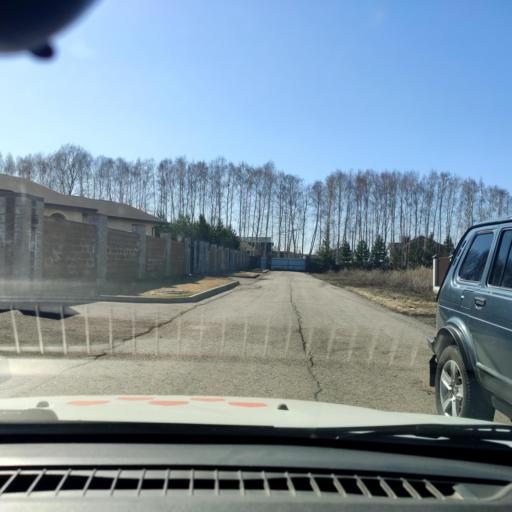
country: RU
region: Bashkortostan
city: Avdon
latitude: 54.4835
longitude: 55.8648
